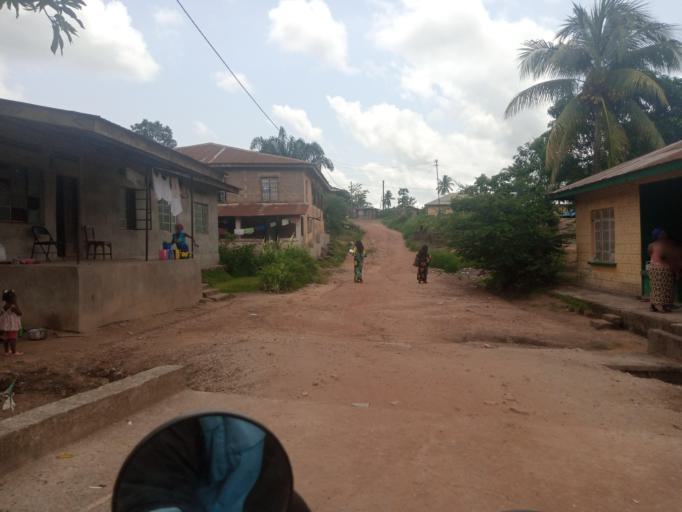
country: SL
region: Southern Province
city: Bo
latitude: 7.9550
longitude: -11.7399
